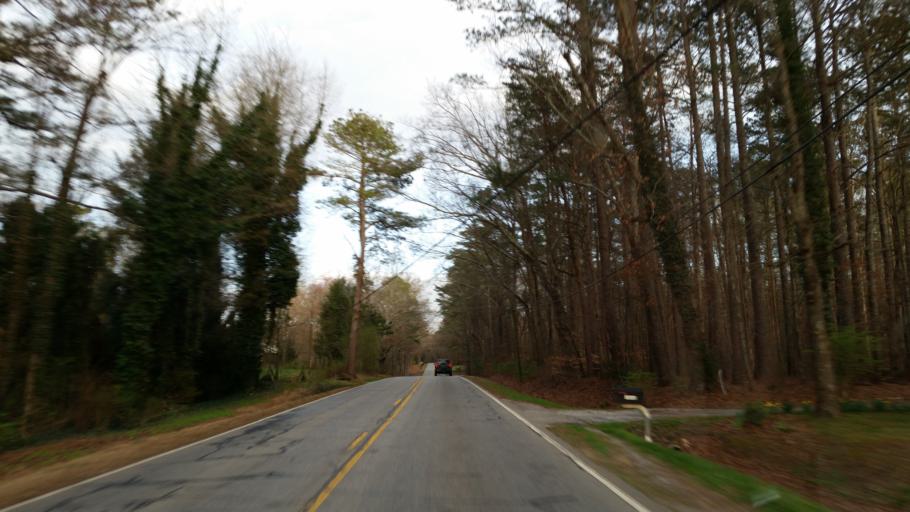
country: US
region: Georgia
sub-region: Pickens County
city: Jasper
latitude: 34.4774
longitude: -84.5715
